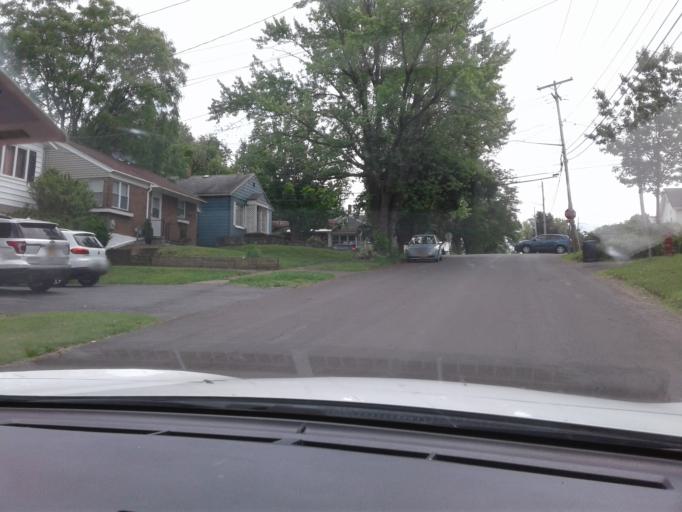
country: US
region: New York
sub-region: Onondaga County
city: East Syracuse
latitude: 43.0675
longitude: -76.0932
